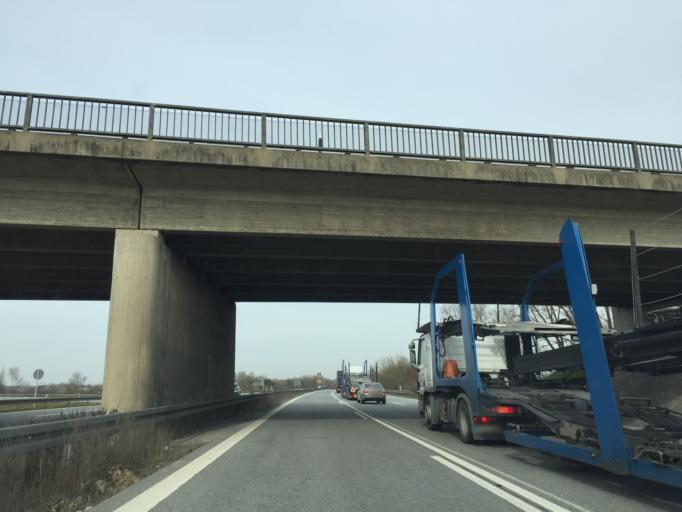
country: AT
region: Upper Austria
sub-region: Politischer Bezirk Scharding
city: Scharding
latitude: 48.4353
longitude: 13.3773
